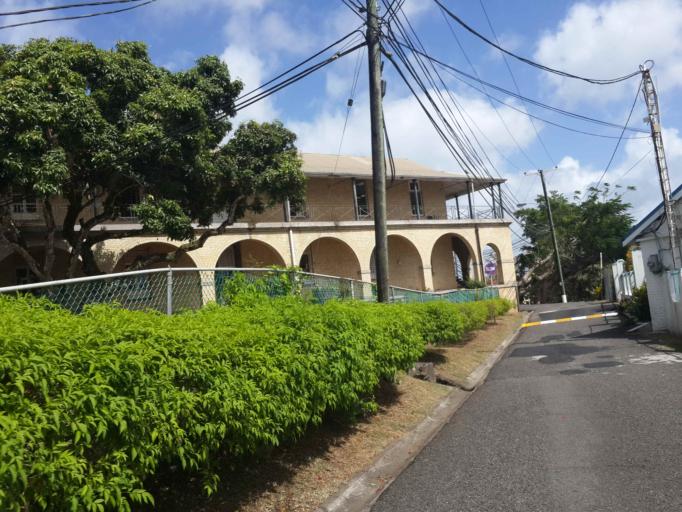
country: LC
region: Castries Quarter
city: Castries
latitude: 13.9988
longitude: -60.9955
